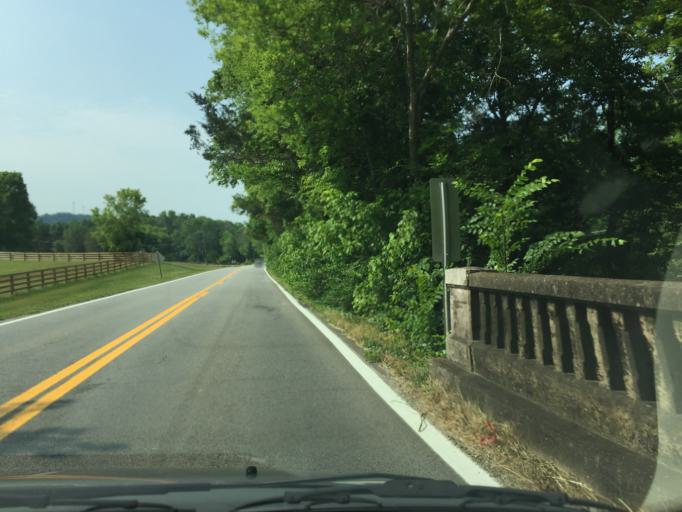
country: US
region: Tennessee
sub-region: Hamilton County
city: East Brainerd
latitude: 34.9912
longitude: -85.0966
